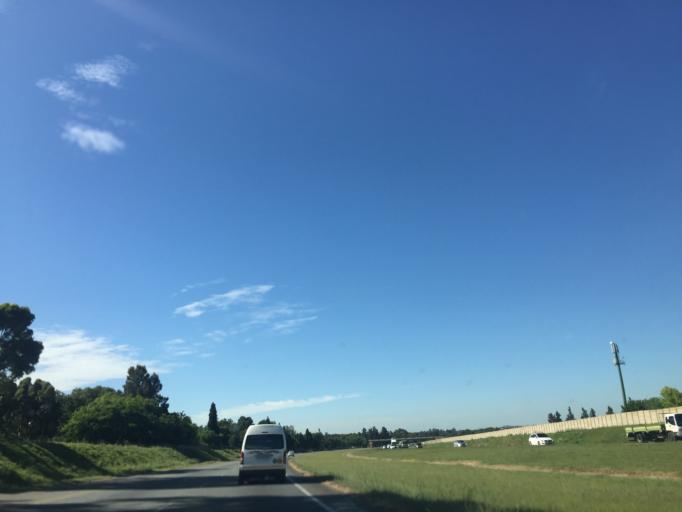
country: ZA
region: Gauteng
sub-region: Ekurhuleni Metropolitan Municipality
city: Germiston
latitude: -26.3246
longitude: 28.1128
